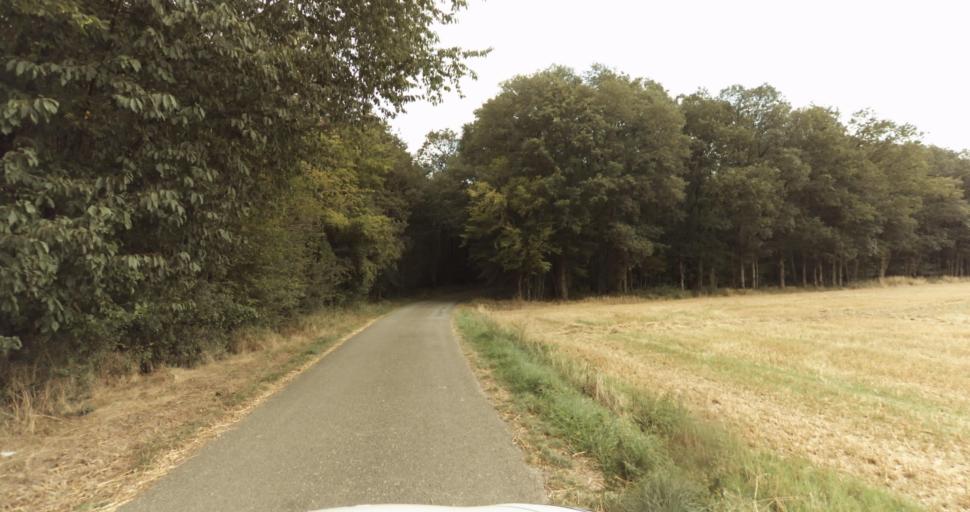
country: FR
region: Haute-Normandie
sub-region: Departement de l'Eure
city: Tillieres-sur-Avre
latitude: 48.7864
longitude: 1.1187
